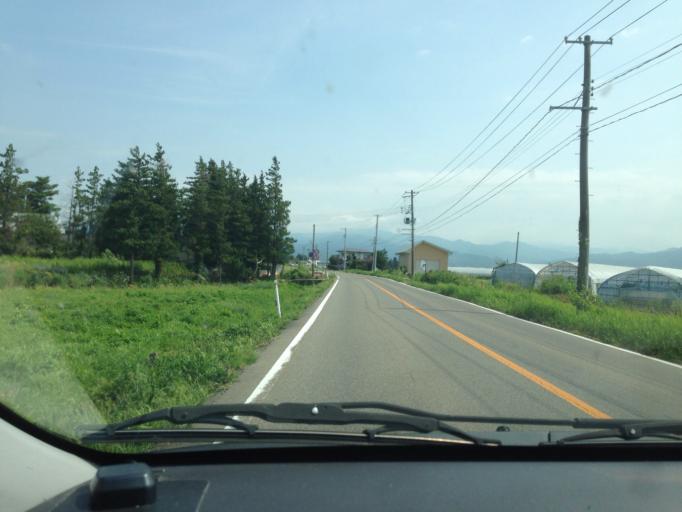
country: JP
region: Fukushima
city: Kitakata
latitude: 37.6147
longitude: 139.8589
